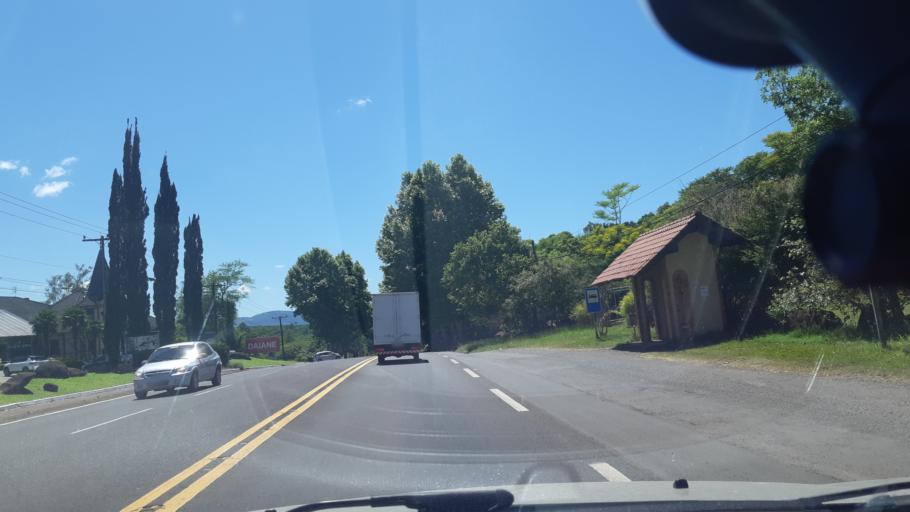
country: BR
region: Rio Grande do Sul
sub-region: Ivoti
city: Ivoti
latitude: -29.6214
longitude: -51.1276
